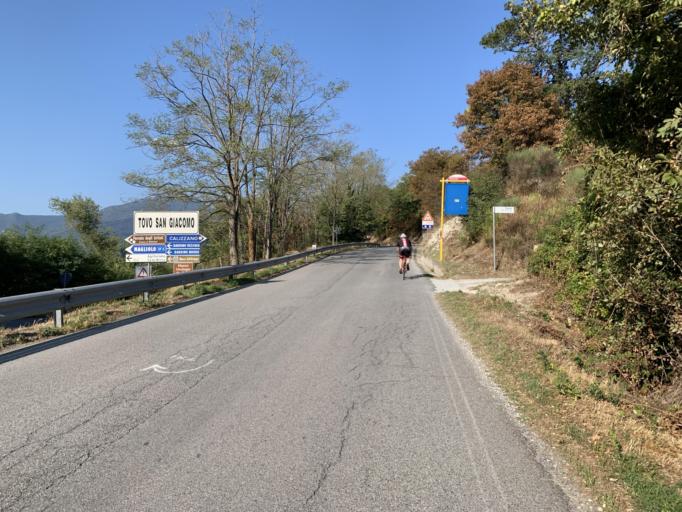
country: IT
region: Liguria
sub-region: Provincia di Savona
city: Calice Ligure
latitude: 44.1952
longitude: 8.2810
